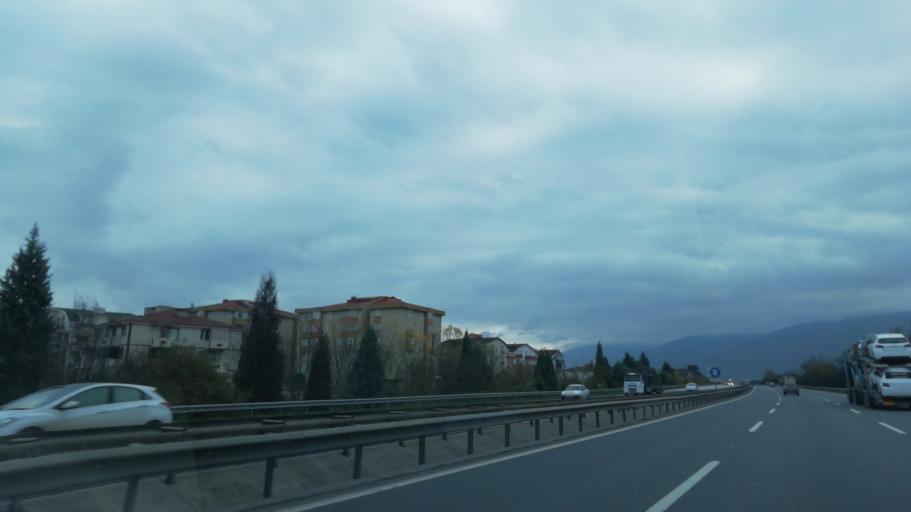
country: TR
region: Kocaeli
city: Kosekoy
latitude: 40.7401
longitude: 30.0457
